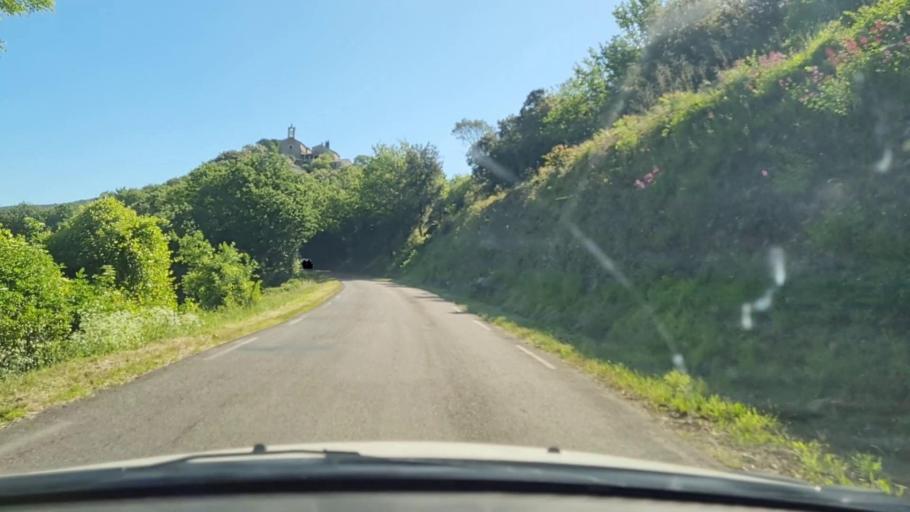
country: FR
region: Languedoc-Roussillon
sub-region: Departement du Gard
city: Cendras
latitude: 44.1494
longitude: 4.0516
